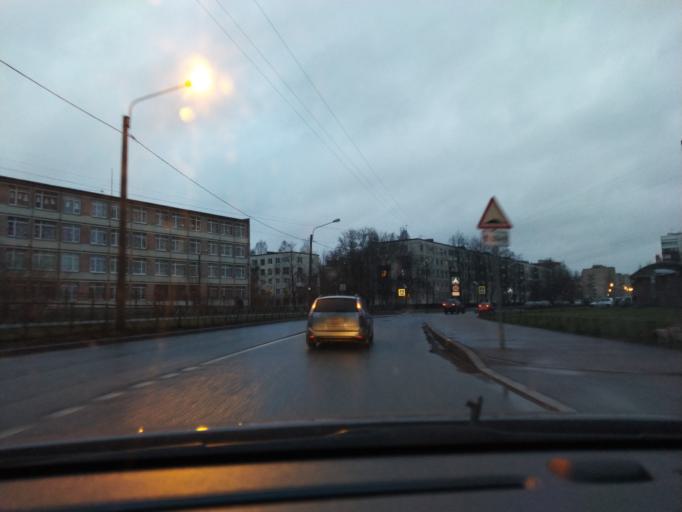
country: RU
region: St.-Petersburg
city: Uritsk
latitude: 59.8280
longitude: 30.1829
